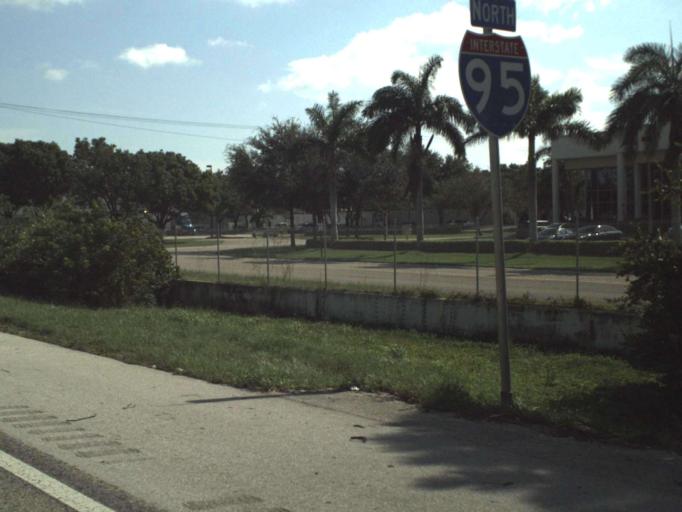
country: US
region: Florida
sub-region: Palm Beach County
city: North Palm Beach
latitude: 26.7918
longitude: -80.0986
